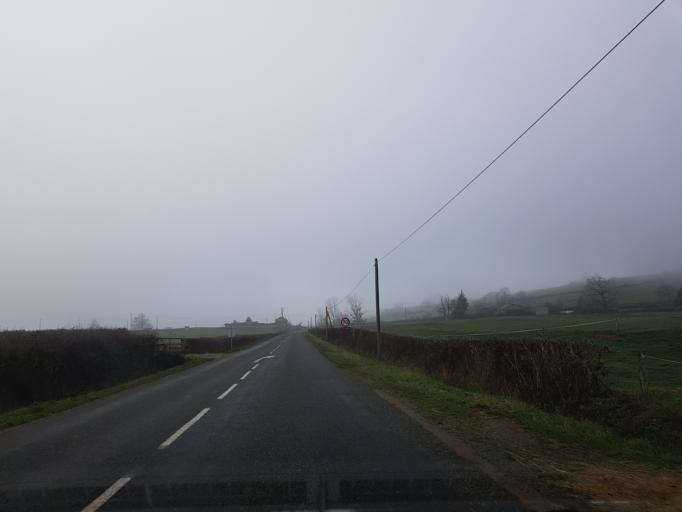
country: FR
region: Bourgogne
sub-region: Departement de Saone-et-Loire
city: Saint-Berain-sous-Sanvignes
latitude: 46.7285
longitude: 4.3028
